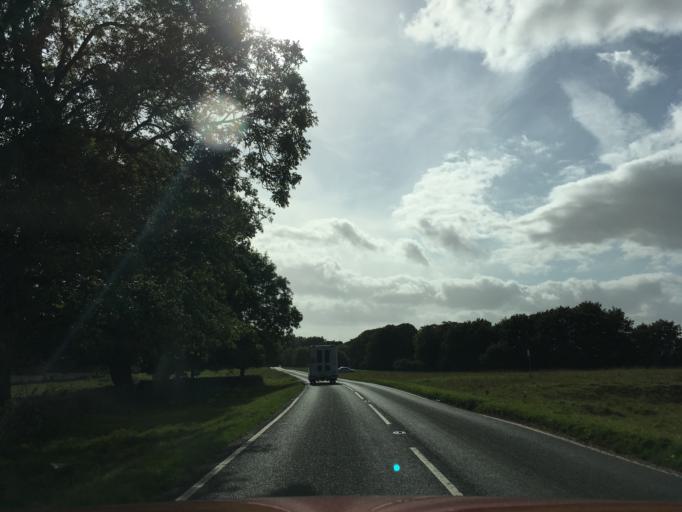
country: GB
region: England
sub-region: Gloucestershire
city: Nailsworth
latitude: 51.7217
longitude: -2.2511
